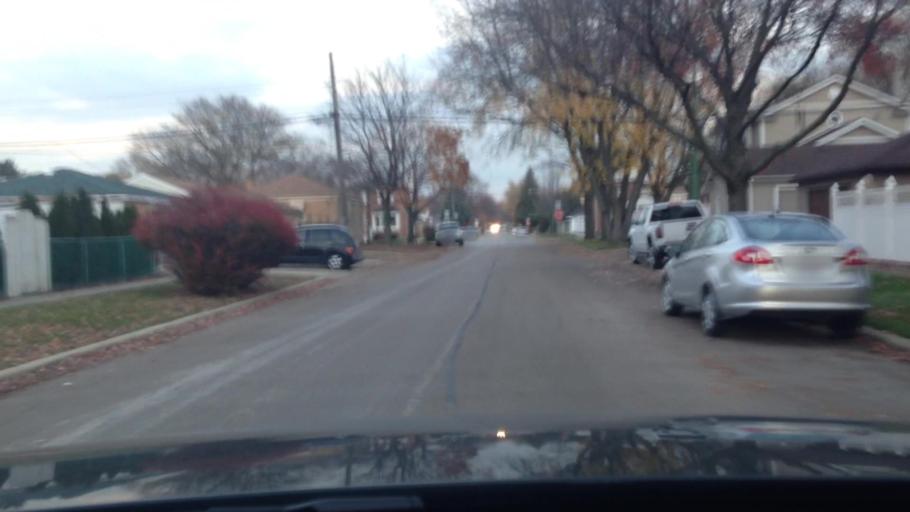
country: US
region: Illinois
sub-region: Cook County
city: Norridge
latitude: 41.9466
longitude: -87.8339
